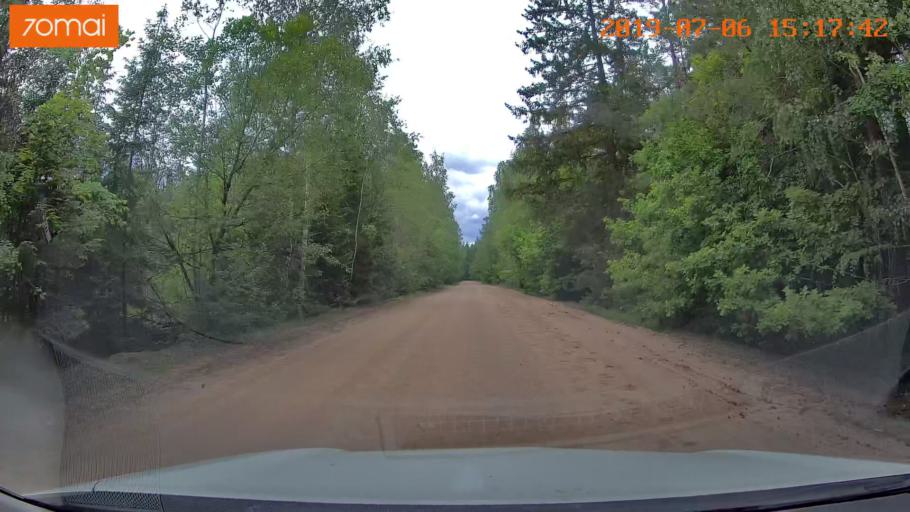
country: BY
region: Minsk
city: Ivyanyets
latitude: 53.9899
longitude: 26.6615
